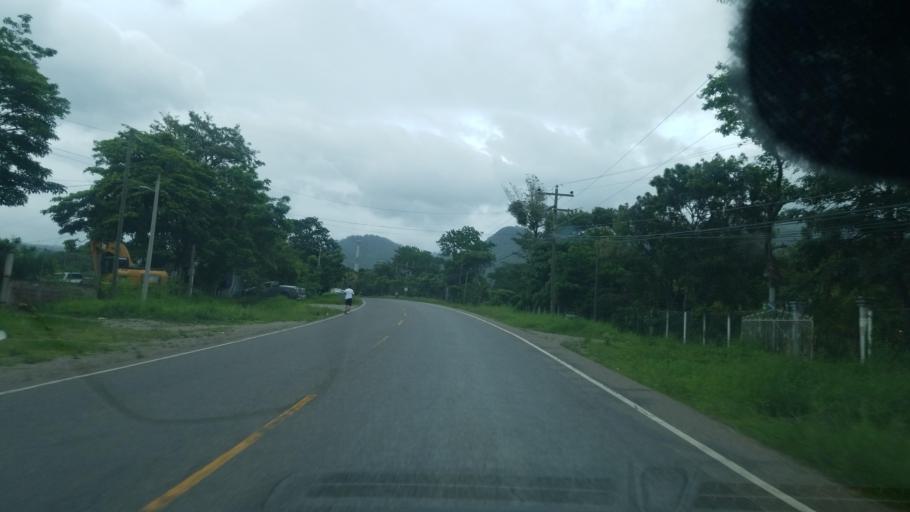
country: HN
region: Ocotepeque
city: Santa Lucia
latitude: 14.4202
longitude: -89.1892
